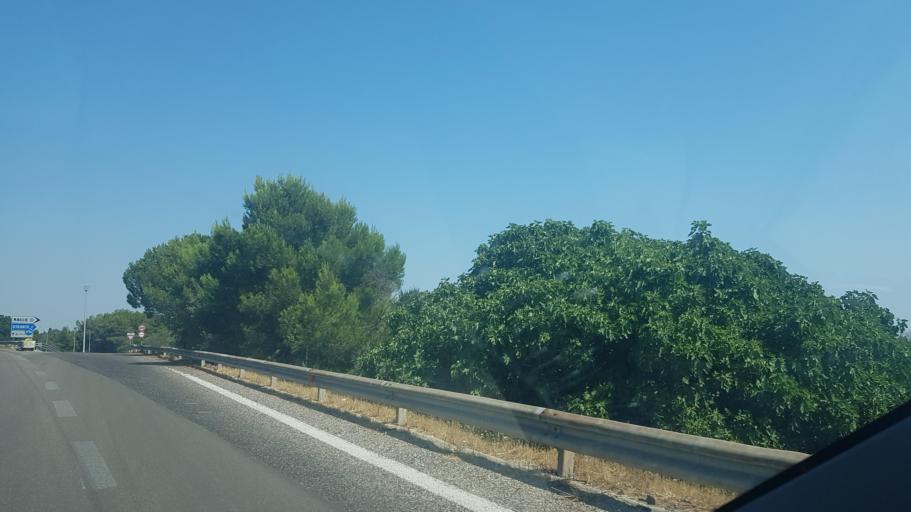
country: IT
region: Apulia
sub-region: Provincia di Lecce
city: Maglie
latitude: 40.1211
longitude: 18.3182
